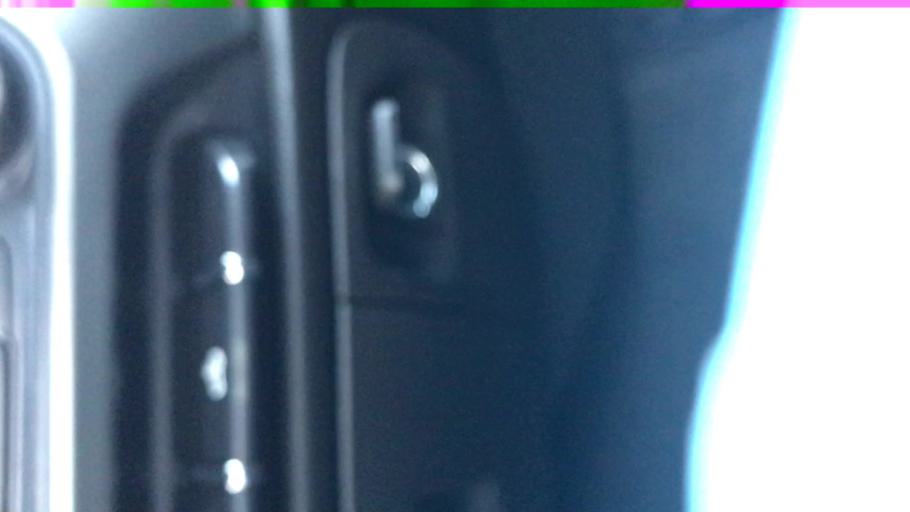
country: US
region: Texas
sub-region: Denton County
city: Double Oak
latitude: 33.0443
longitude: -97.1098
